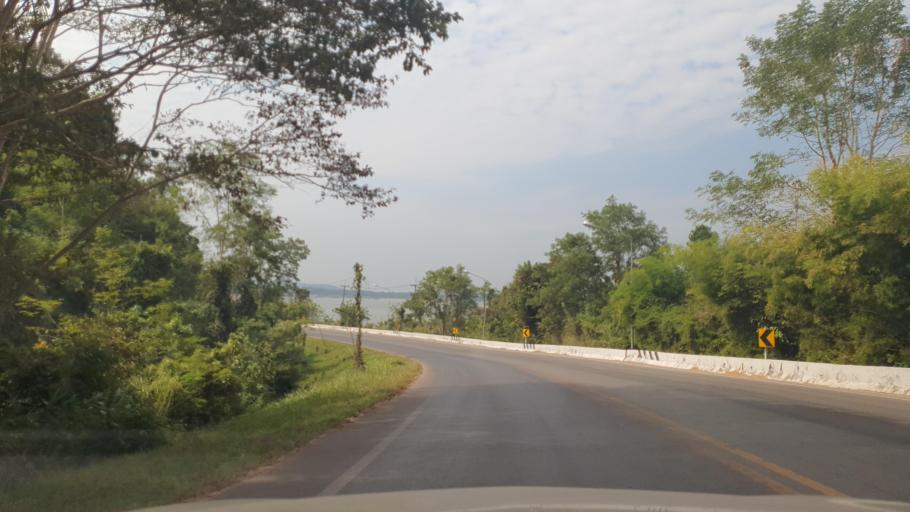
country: TH
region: Changwat Bueng Kan
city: Bung Khla
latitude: 18.2909
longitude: 103.8891
